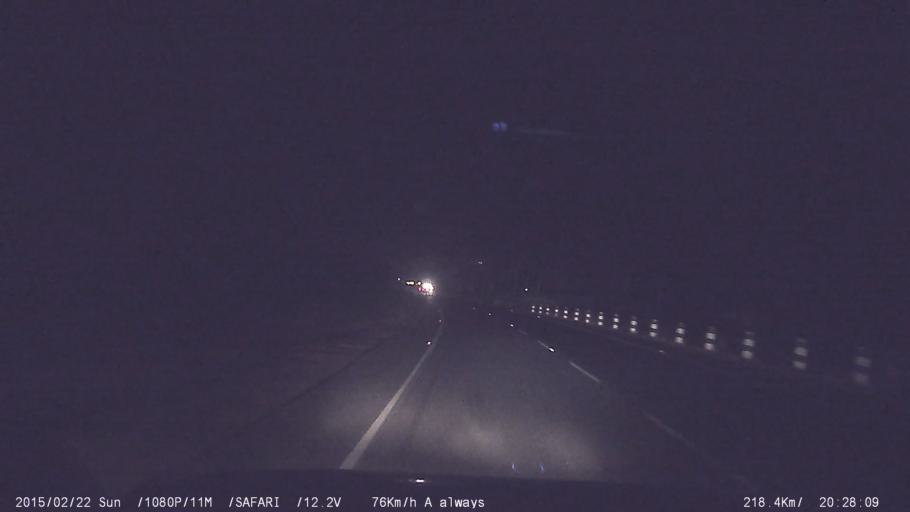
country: IN
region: Tamil Nadu
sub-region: Dindigul
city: Dindigul
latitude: 10.3264
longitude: 77.9186
